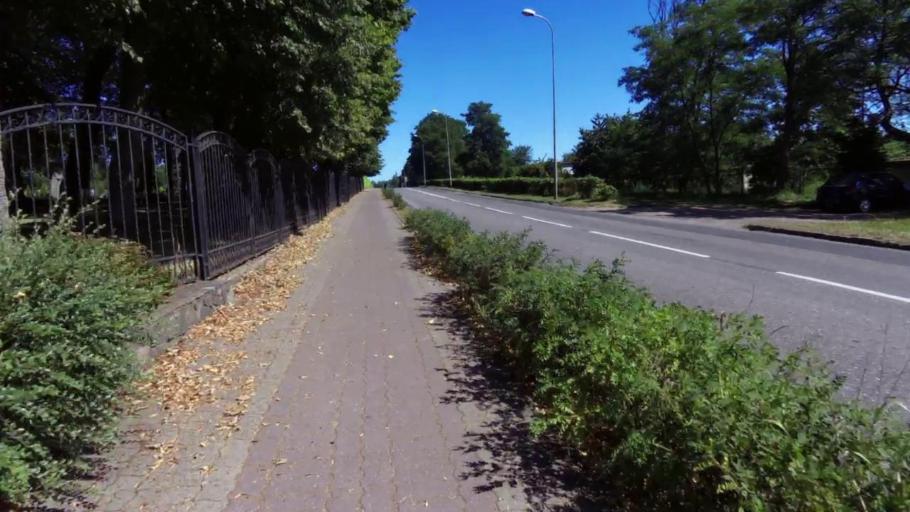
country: PL
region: West Pomeranian Voivodeship
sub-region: Powiat drawski
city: Czaplinek
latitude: 53.5611
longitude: 16.2373
